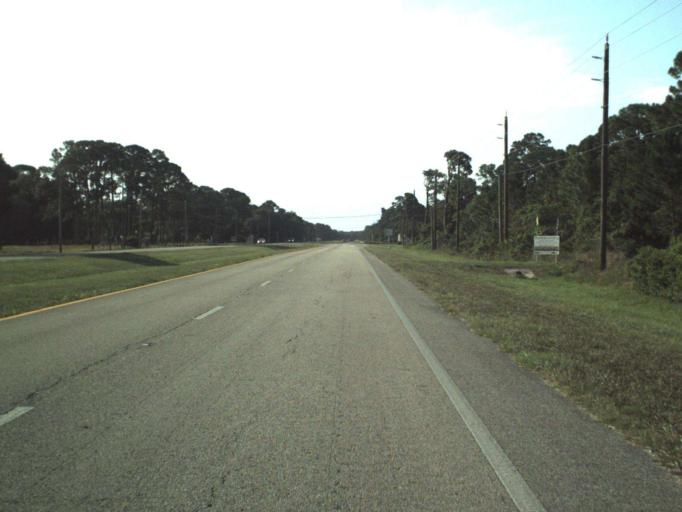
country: US
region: Florida
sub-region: Volusia County
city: Oak Hill
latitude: 28.8801
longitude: -80.8543
